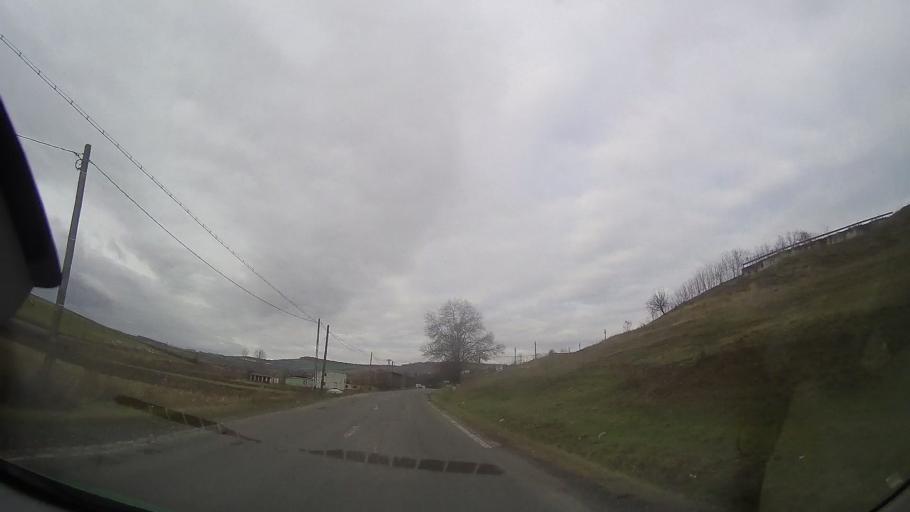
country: RO
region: Bistrita-Nasaud
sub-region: Comuna Urmenis
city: Urmenis
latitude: 46.7652
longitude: 24.3729
